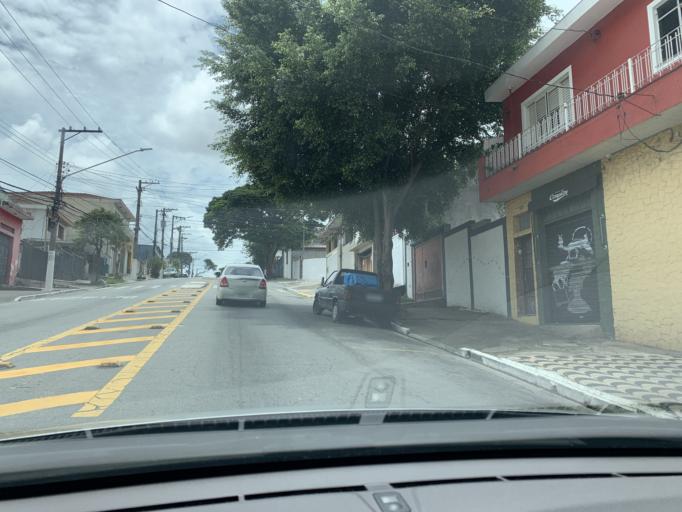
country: BR
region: Sao Paulo
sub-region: Sao Paulo
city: Sao Paulo
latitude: -23.4994
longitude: -46.6838
